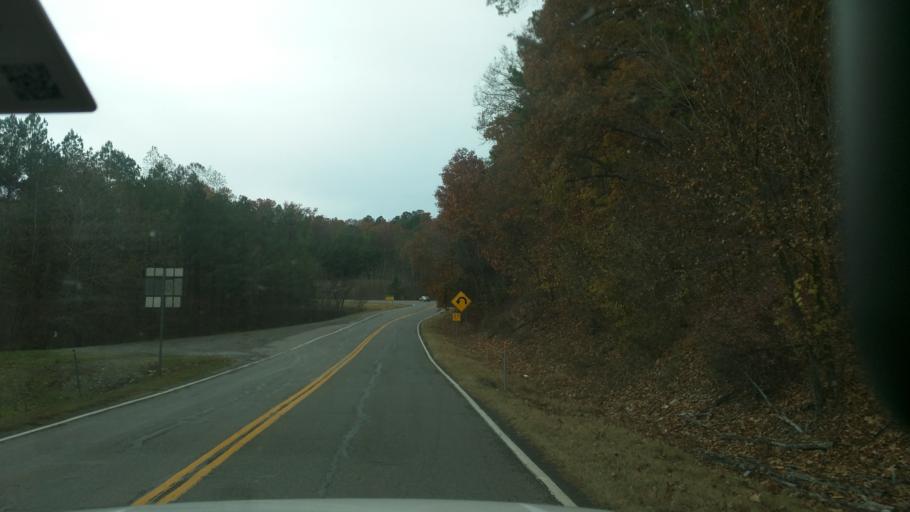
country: US
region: Oklahoma
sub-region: Cherokee County
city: Tahlequah
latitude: 35.9286
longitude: -94.8421
